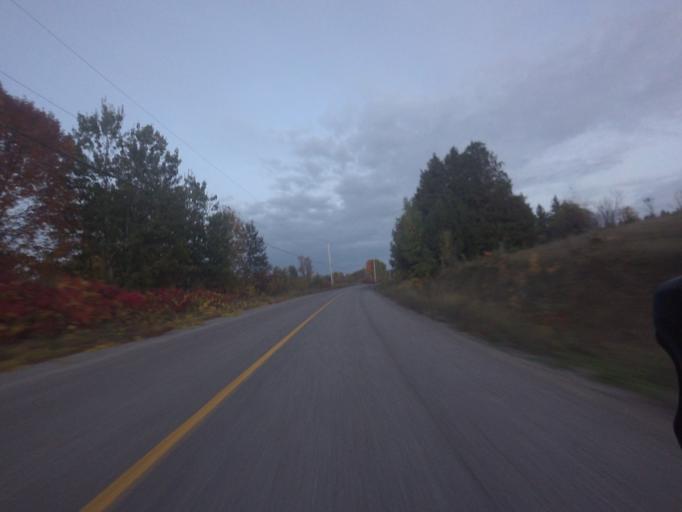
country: CA
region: Ontario
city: Renfrew
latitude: 45.3450
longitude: -76.9309
